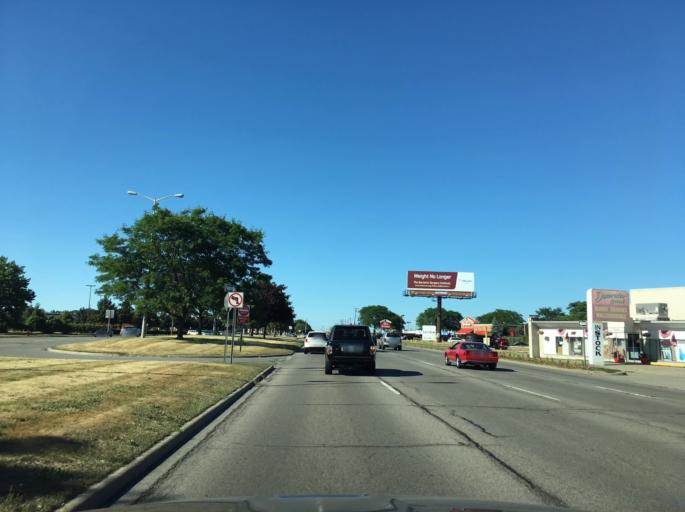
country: US
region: Michigan
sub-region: Macomb County
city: Roseville
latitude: 42.5210
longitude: -82.9211
